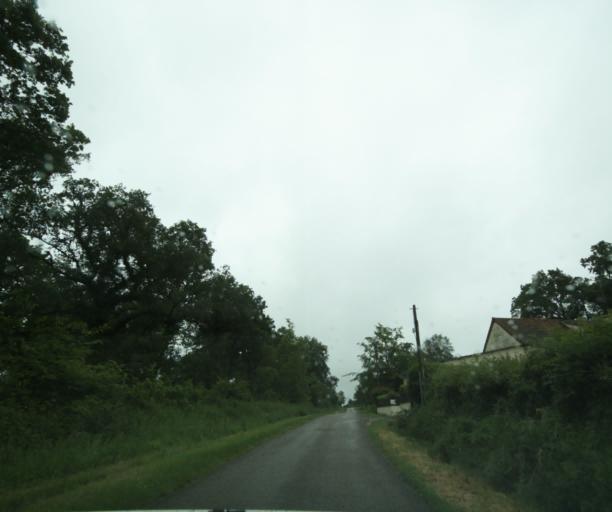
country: FR
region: Bourgogne
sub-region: Departement de Saone-et-Loire
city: Charolles
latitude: 46.4212
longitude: 4.3002
